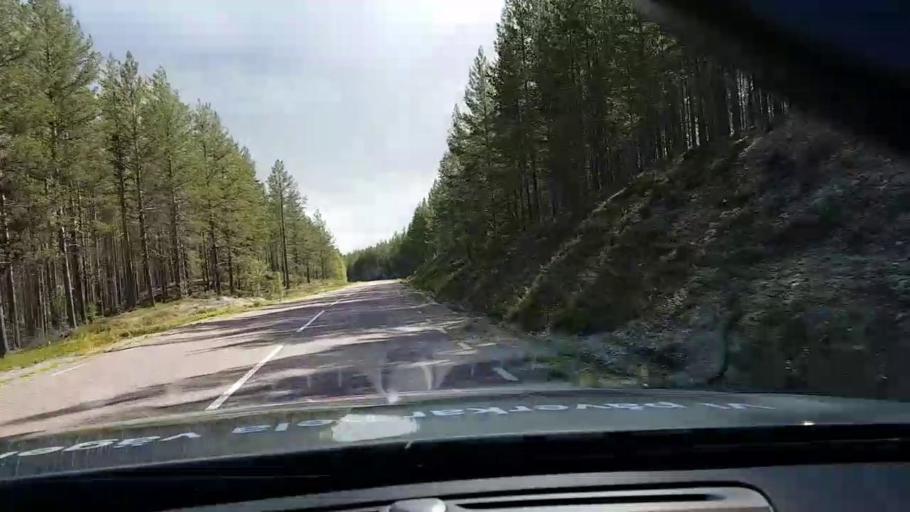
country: SE
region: Vaesterbotten
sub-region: Asele Kommun
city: Asele
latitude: 63.8824
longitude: 17.3540
